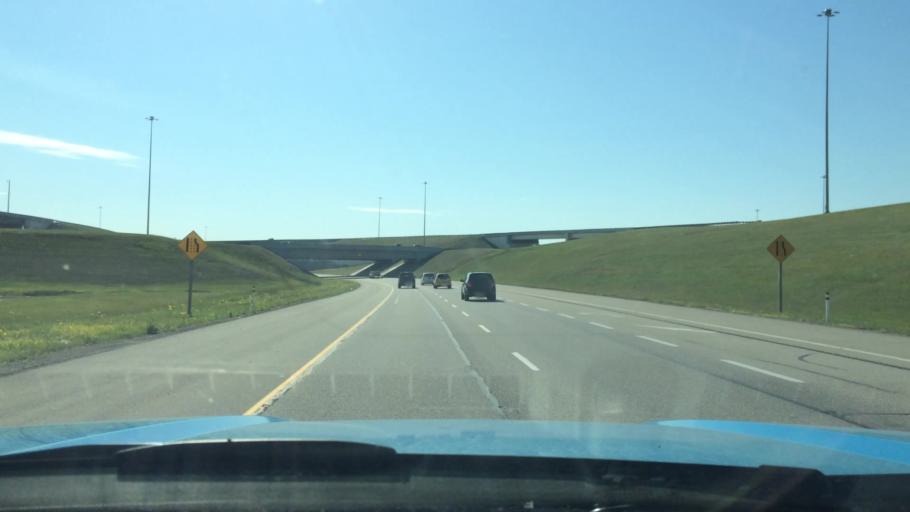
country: CA
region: Alberta
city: Airdrie
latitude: 51.1748
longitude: -114.0050
